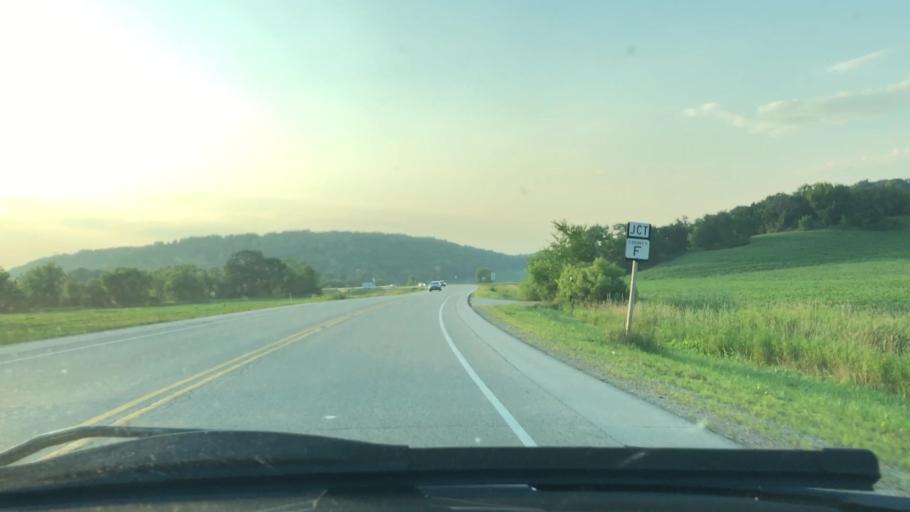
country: US
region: Wisconsin
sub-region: Dane County
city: Black Earth
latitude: 43.1383
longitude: -89.7401
